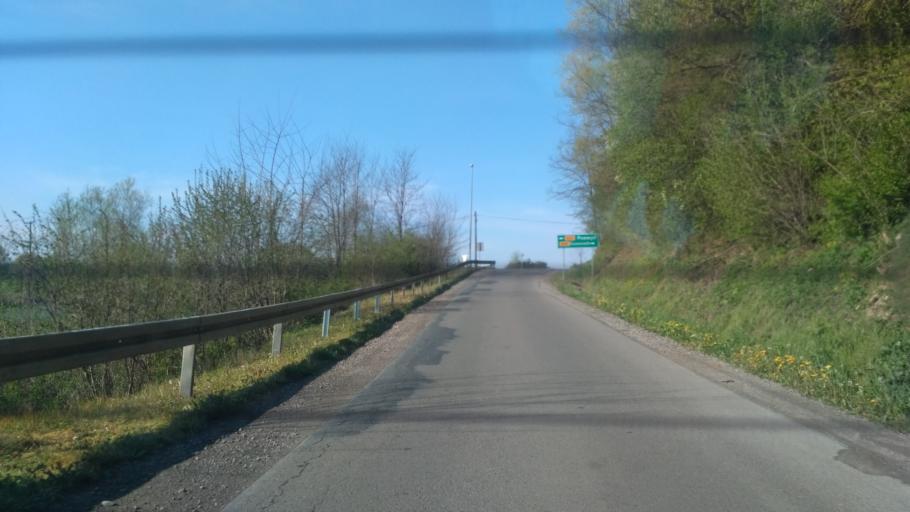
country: PL
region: Subcarpathian Voivodeship
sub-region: Powiat jaroslawski
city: Kramarzowka
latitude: 49.8154
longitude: 22.4892
